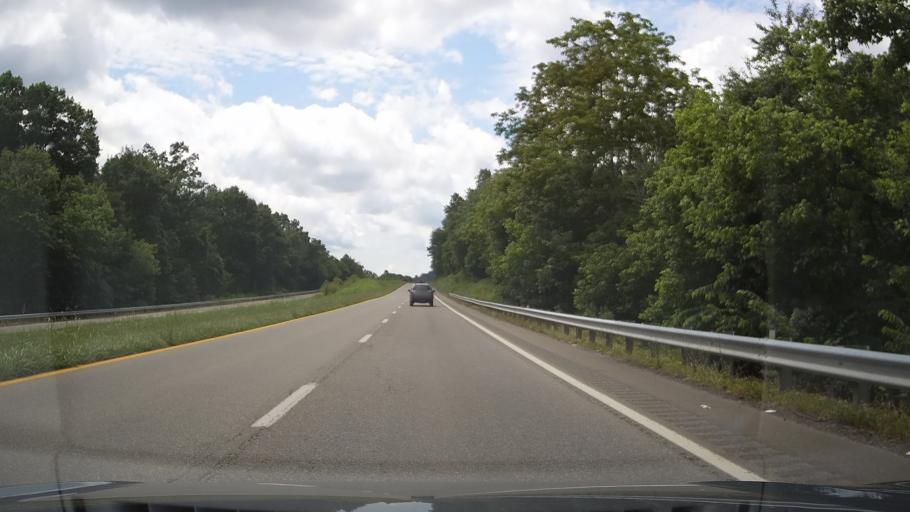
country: US
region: Virginia
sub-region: Scott County
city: Gate City
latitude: 36.6355
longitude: -82.6431
